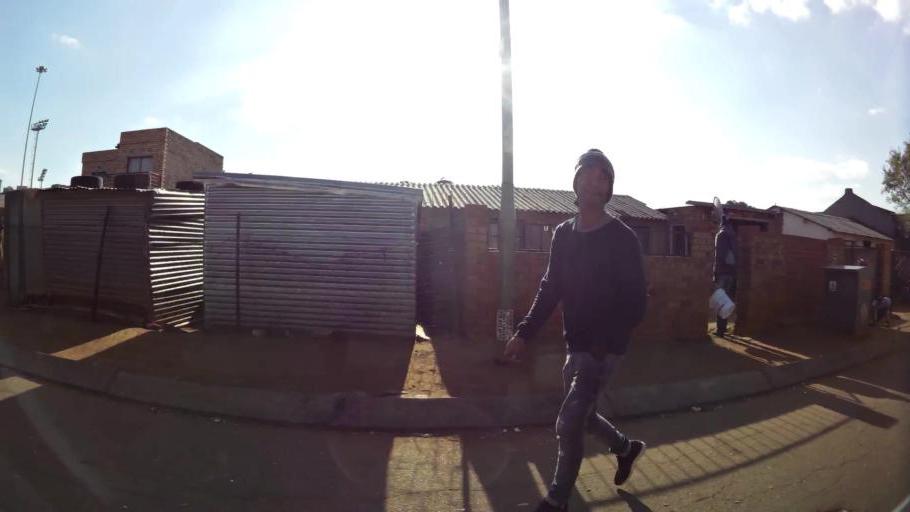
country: ZA
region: Gauteng
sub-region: City of Johannesburg Metropolitan Municipality
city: Soweto
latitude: -26.2584
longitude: 27.9133
